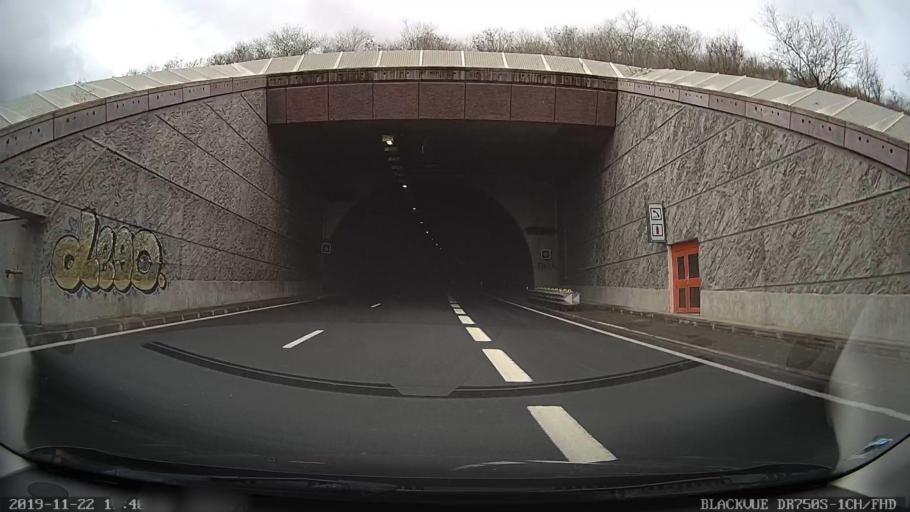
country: RE
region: Reunion
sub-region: Reunion
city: Saint-Paul
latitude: -21.0283
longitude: 55.2545
